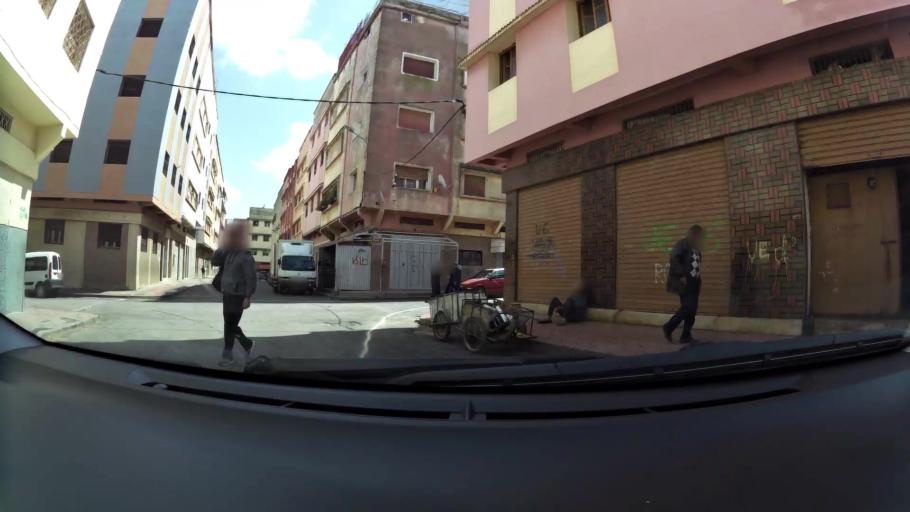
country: MA
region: Grand Casablanca
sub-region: Casablanca
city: Casablanca
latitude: 33.5365
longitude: -7.5677
